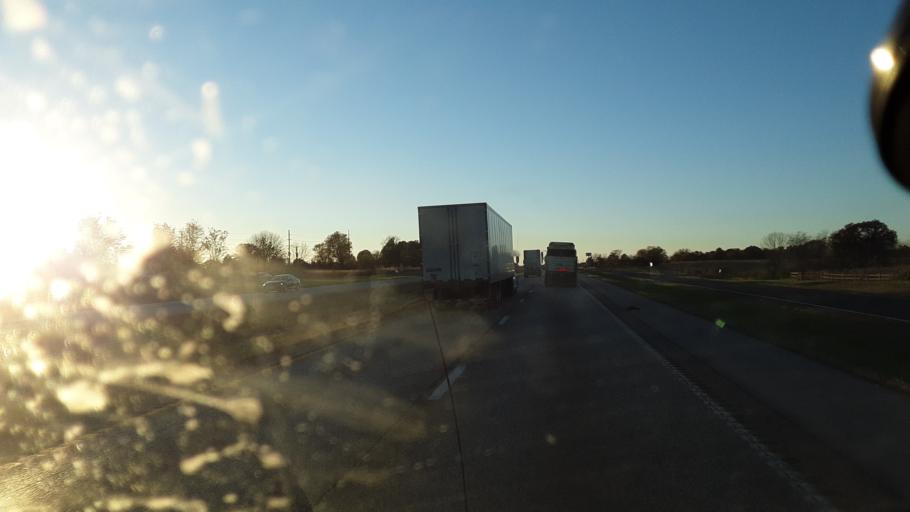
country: US
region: Missouri
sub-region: Warren County
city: Wright City
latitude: 38.8189
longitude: -90.9679
